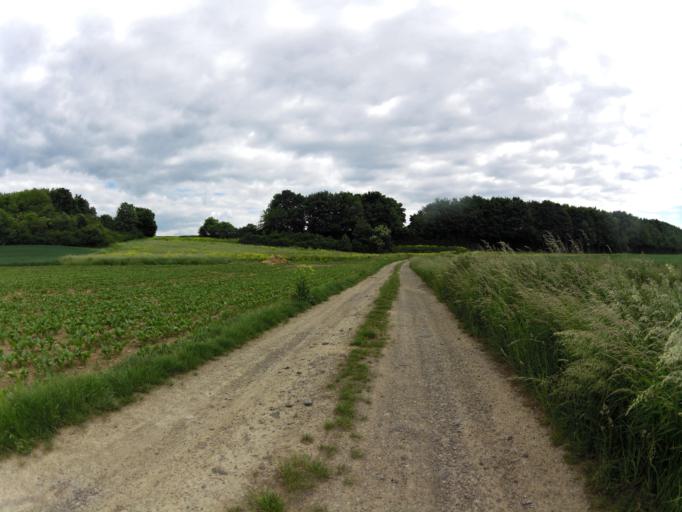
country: DE
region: Bavaria
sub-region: Regierungsbezirk Unterfranken
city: Gaukonigshofen
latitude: 49.6622
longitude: 10.0028
